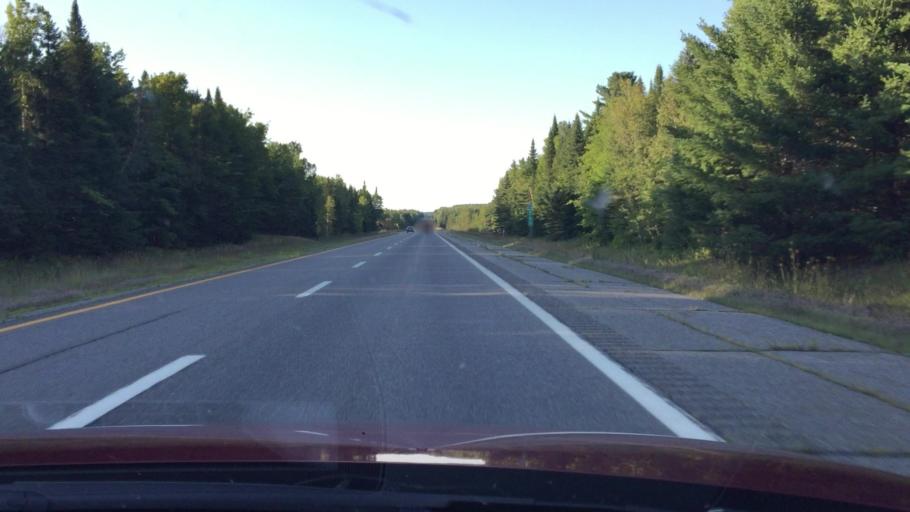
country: US
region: Maine
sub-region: Penobscot County
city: Patten
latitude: 45.8154
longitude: -68.4293
